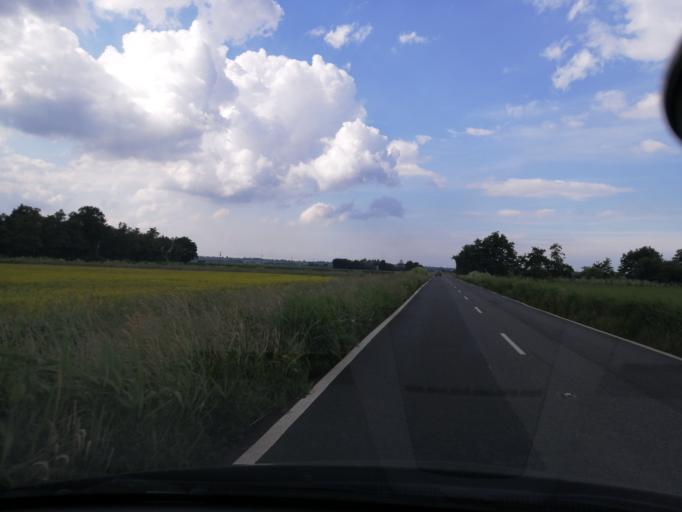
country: GB
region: England
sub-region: Cambridgeshire
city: Yaxley
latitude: 52.4873
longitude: -0.2432
